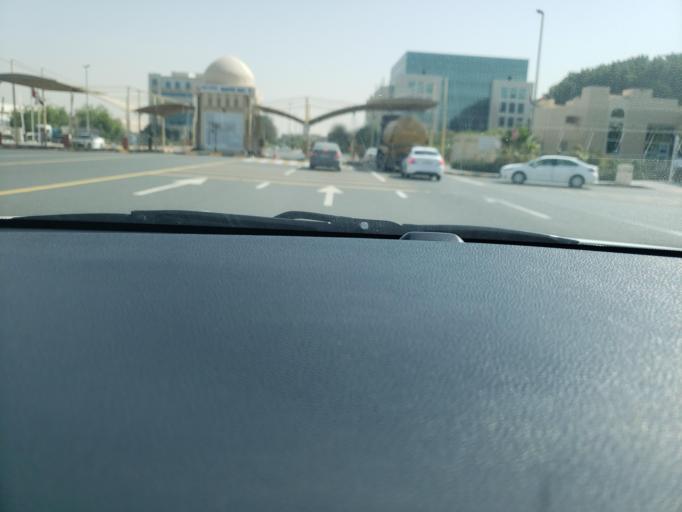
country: AE
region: Ash Shariqah
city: Sharjah
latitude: 25.3269
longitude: 55.4950
